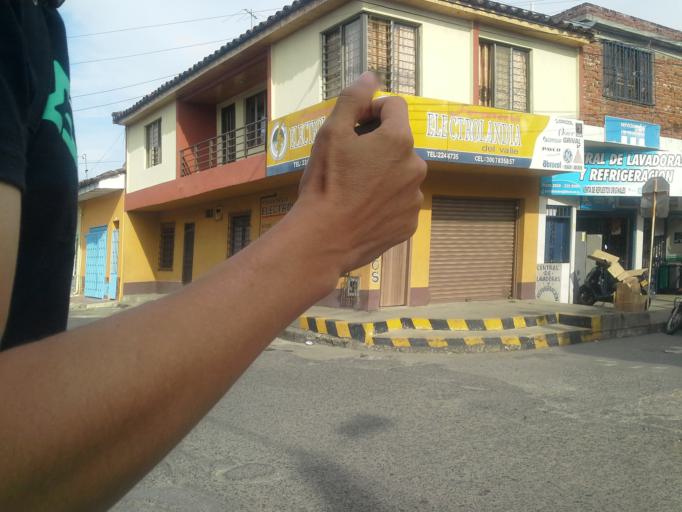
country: CO
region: Valle del Cauca
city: Tulua
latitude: 4.0880
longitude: -76.1981
